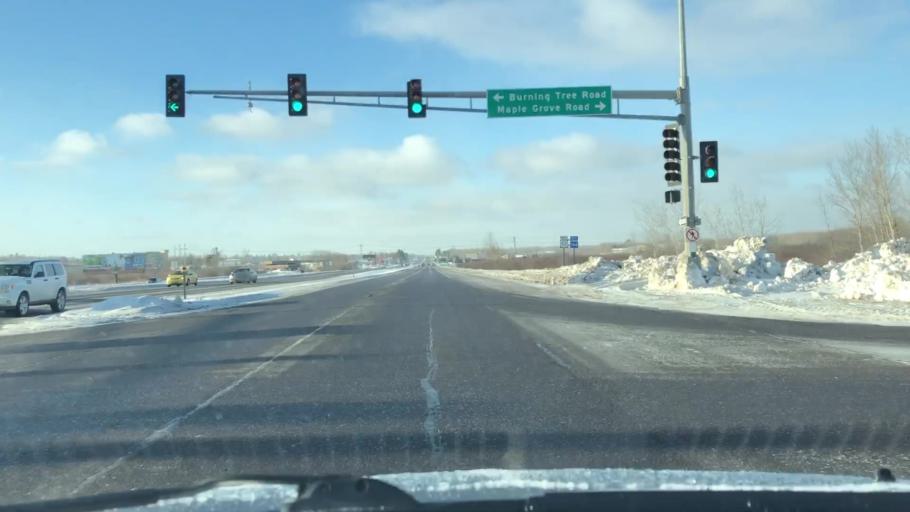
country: US
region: Minnesota
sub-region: Saint Louis County
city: Duluth
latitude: 46.8109
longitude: -92.1682
